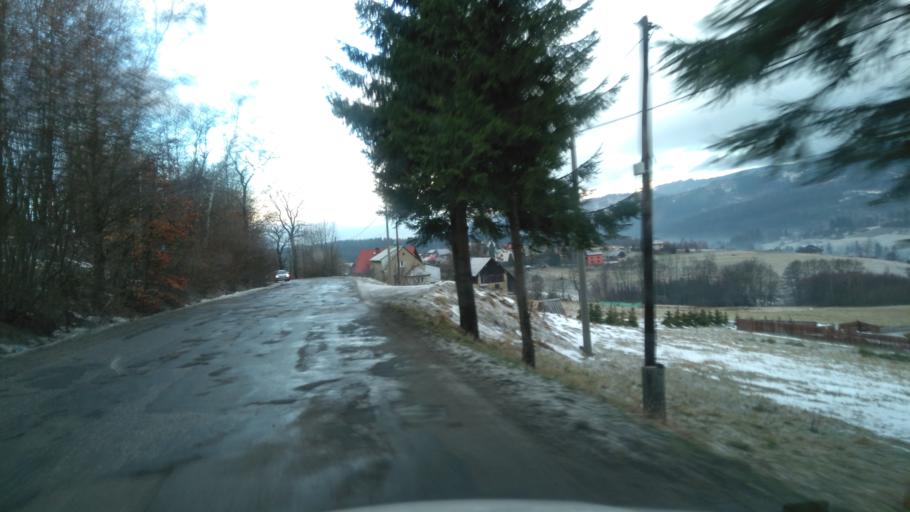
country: PL
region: Silesian Voivodeship
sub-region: Powiat cieszynski
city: Istebna
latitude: 49.5500
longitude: 18.8957
